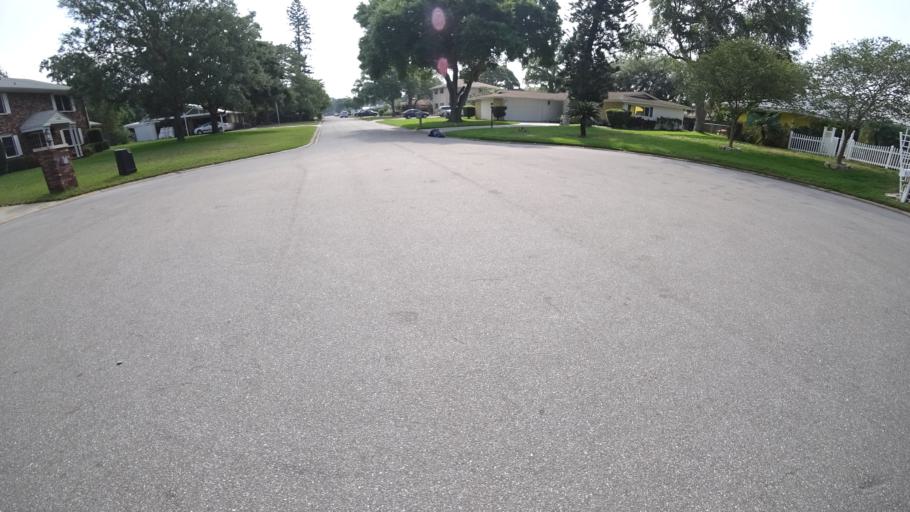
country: US
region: Florida
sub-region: Manatee County
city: West Bradenton
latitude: 27.4918
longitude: -82.6161
